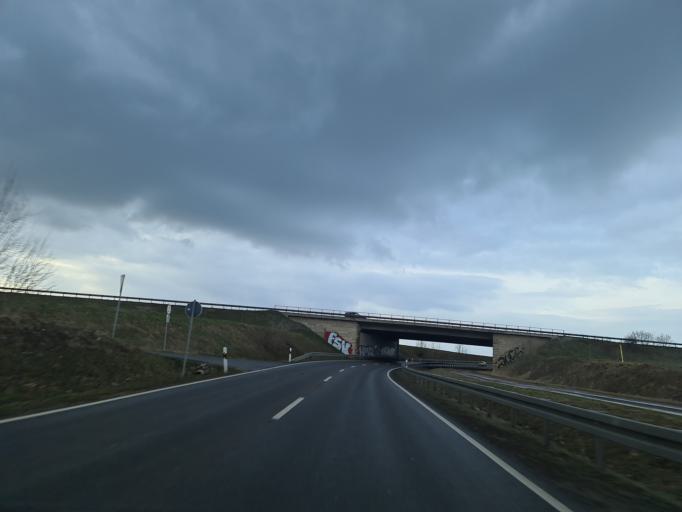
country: DE
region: Saxony
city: Reinsdorf
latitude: 50.6830
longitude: 12.5905
